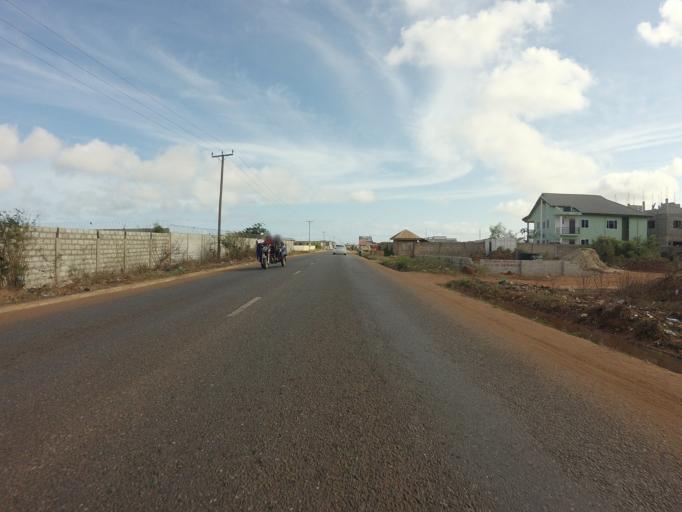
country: GH
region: Greater Accra
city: Teshi Old Town
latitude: 5.5942
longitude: -0.1363
